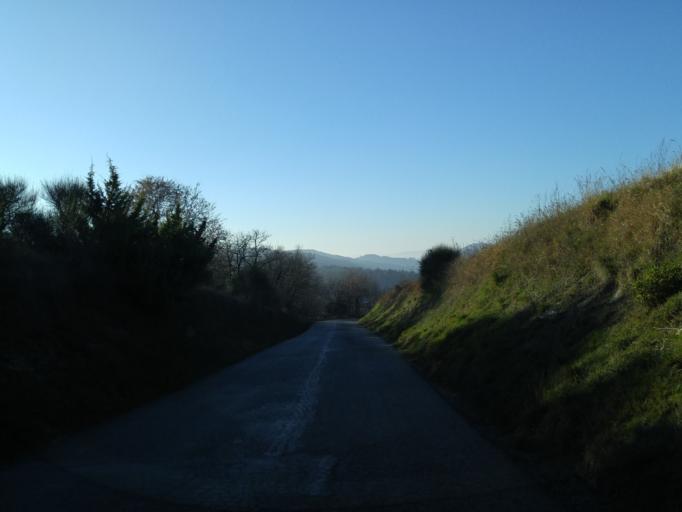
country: IT
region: The Marches
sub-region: Provincia di Pesaro e Urbino
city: Isola del Piano
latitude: 43.7174
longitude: 12.7487
